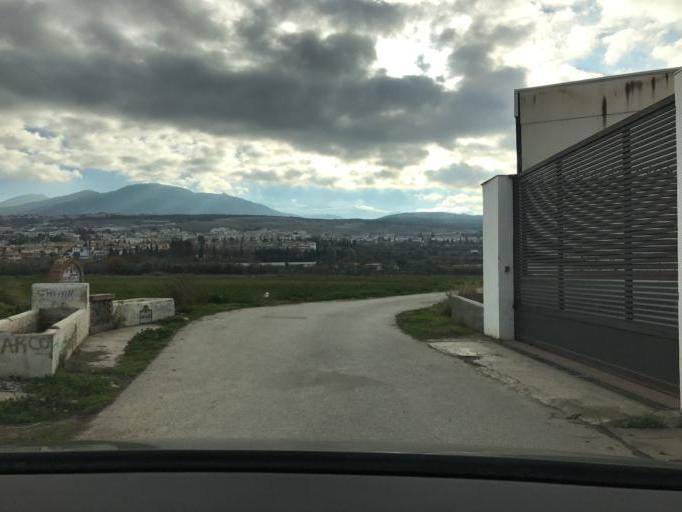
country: ES
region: Andalusia
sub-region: Provincia de Granada
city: Cajar
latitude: 37.1324
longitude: -3.5807
